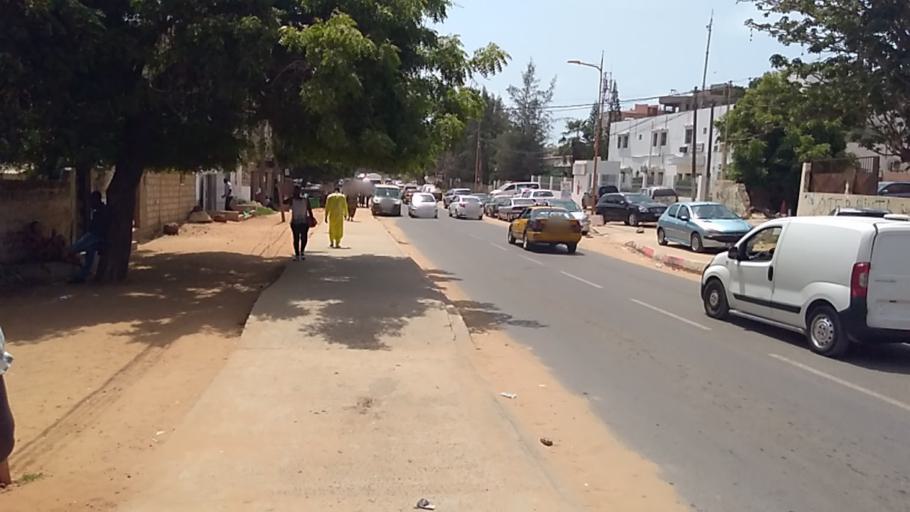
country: SN
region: Dakar
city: Mermoz Boabab
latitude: 14.7217
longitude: -17.4918
